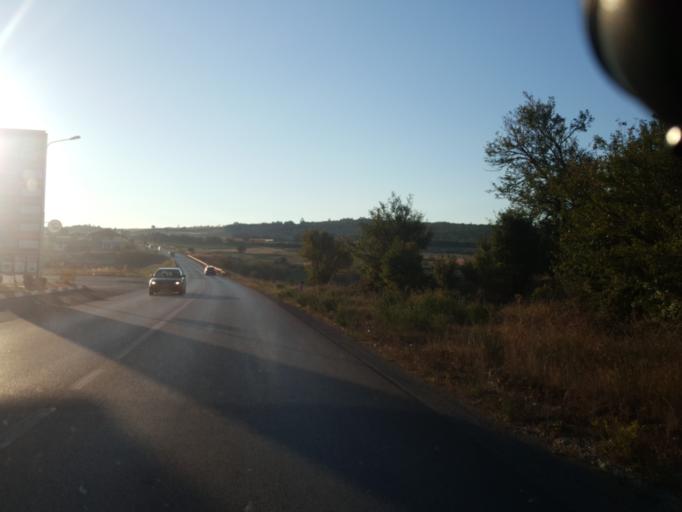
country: XK
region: Pec
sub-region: Komuna e Klines
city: Klina
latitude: 42.5897
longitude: 20.6668
